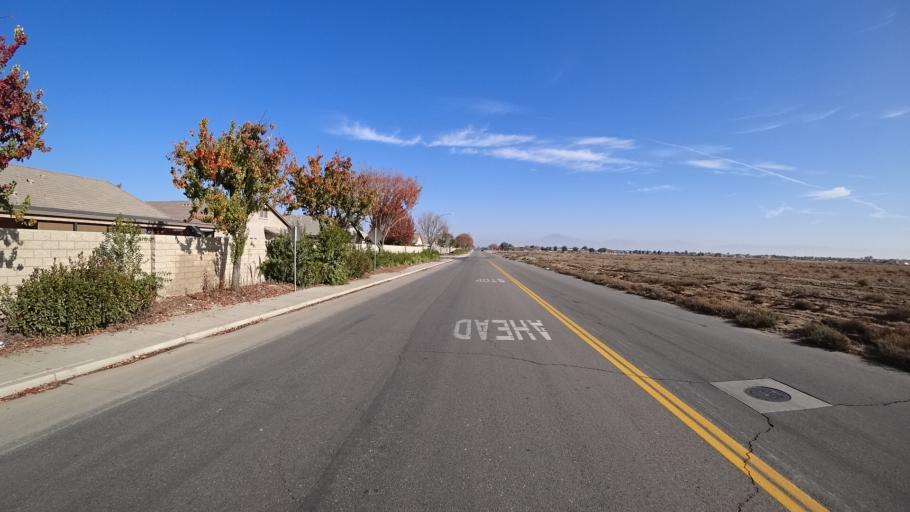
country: US
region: California
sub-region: Kern County
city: Greenfield
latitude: 35.2888
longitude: -119.0731
